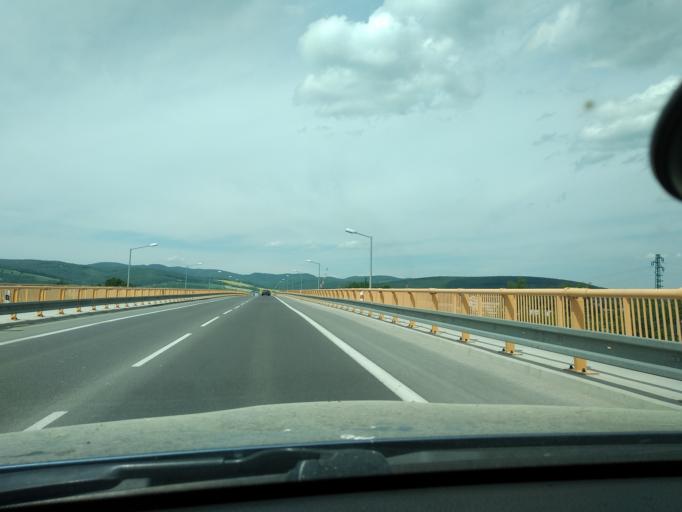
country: SK
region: Trenciansky
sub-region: Okres Trencin
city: Trencin
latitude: 48.8826
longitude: 18.0130
